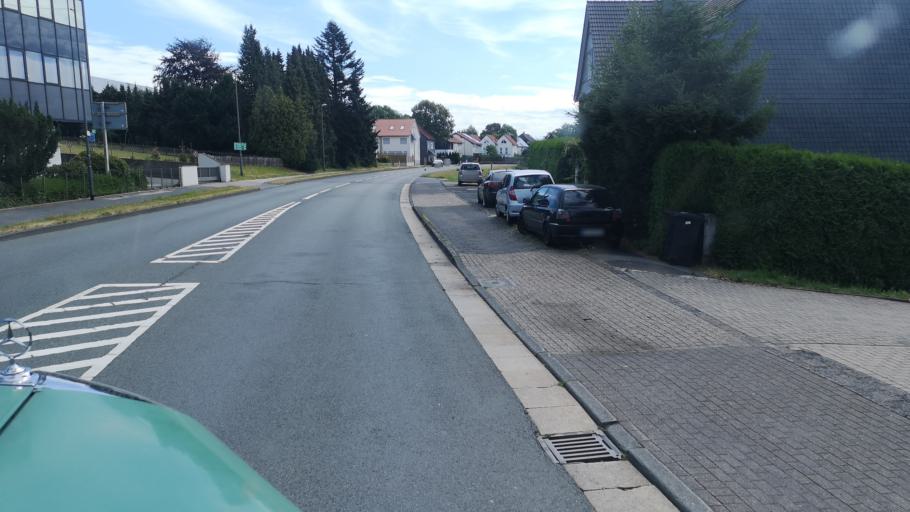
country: DE
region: North Rhine-Westphalia
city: Radevormwald
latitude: 51.2004
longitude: 7.3700
